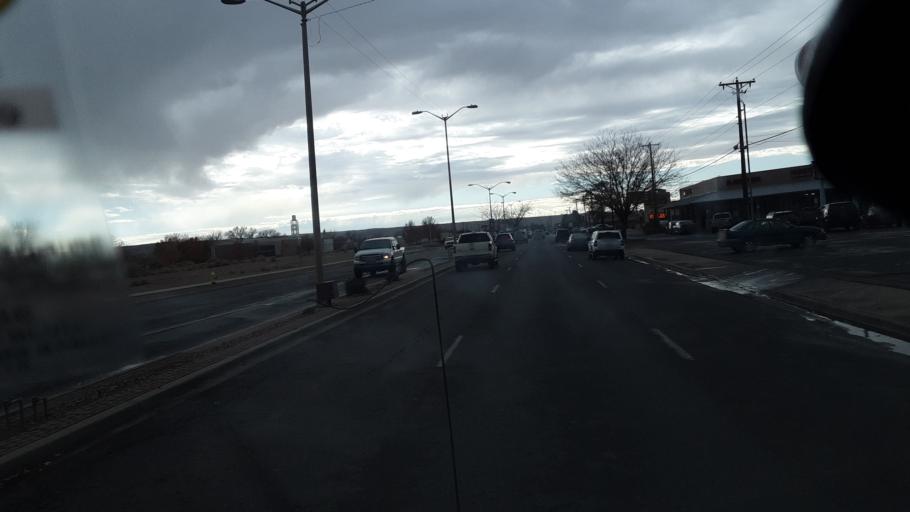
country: US
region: New Mexico
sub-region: San Juan County
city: Farmington
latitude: 36.7473
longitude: -108.1626
